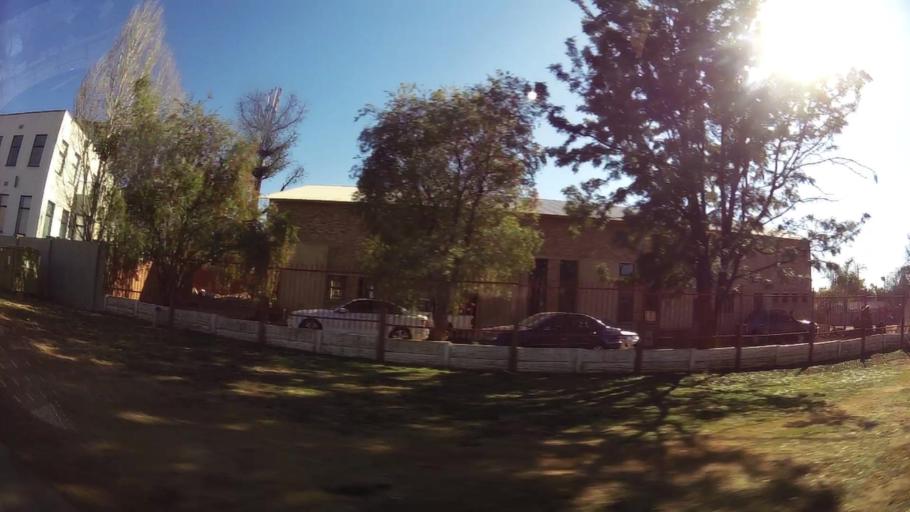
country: ZA
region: Gauteng
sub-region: City of Tshwane Metropolitan Municipality
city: Centurion
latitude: -25.8437
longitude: 28.2105
